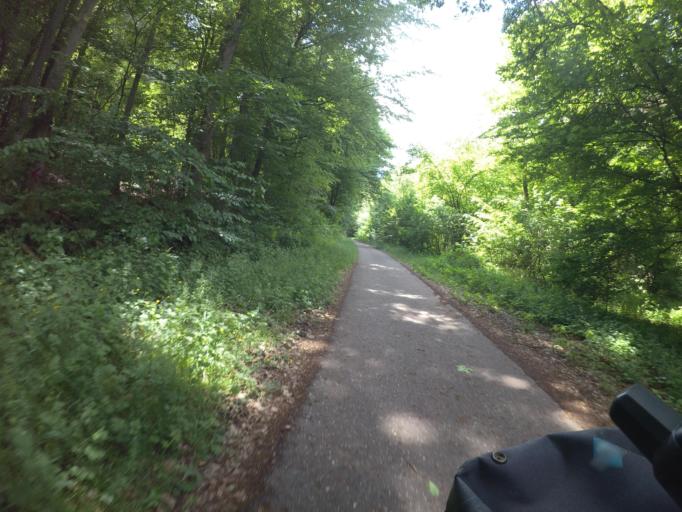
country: DE
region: Rheinland-Pfalz
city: Rumbach
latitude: 49.0834
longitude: 7.7889
